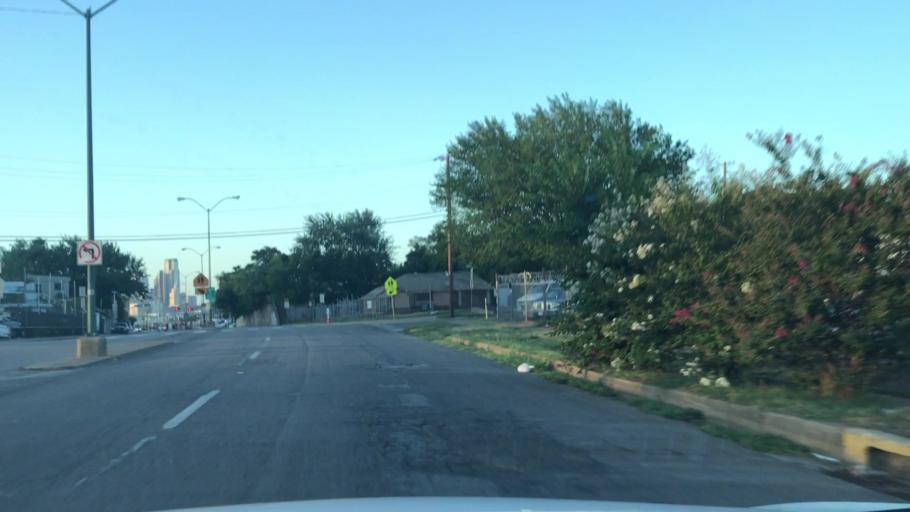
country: US
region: Texas
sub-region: Dallas County
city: Dallas
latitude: 32.7493
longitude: -96.8126
